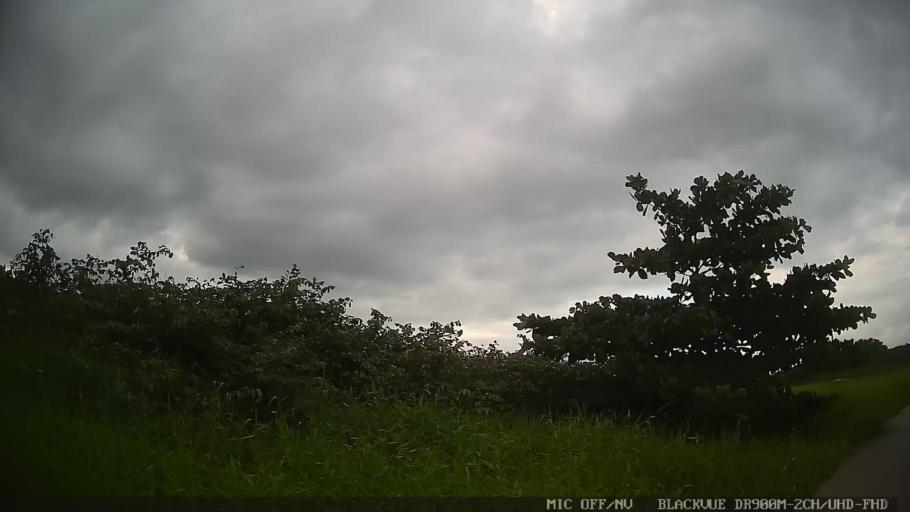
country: BR
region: Sao Paulo
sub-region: Itanhaem
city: Itanhaem
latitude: -24.2297
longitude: -46.8654
